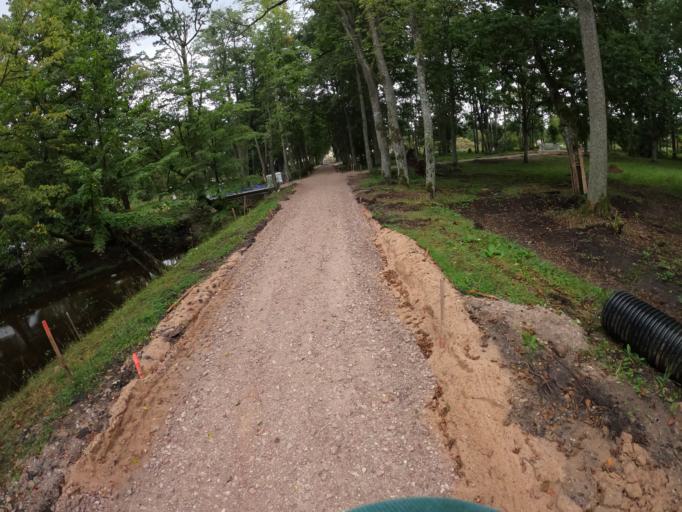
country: LV
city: Tireli
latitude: 56.9476
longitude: 23.4963
